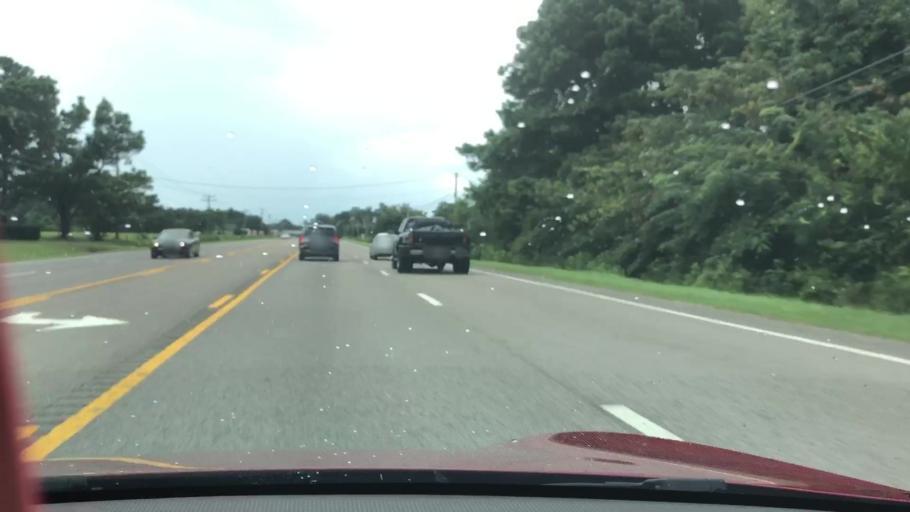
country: US
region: North Carolina
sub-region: Dare County
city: Southern Shores
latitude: 36.1318
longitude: -75.8401
